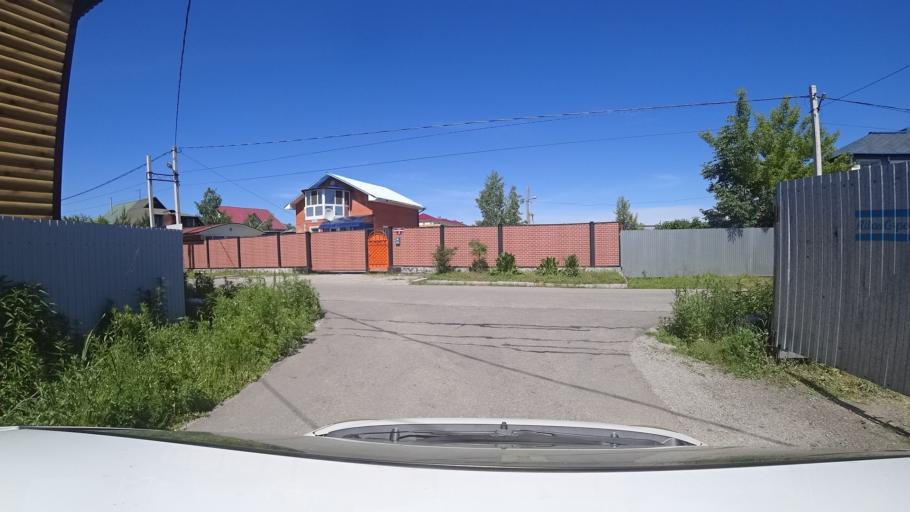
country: RU
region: Khabarovsk Krai
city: Topolevo
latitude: 48.5041
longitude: 135.1755
